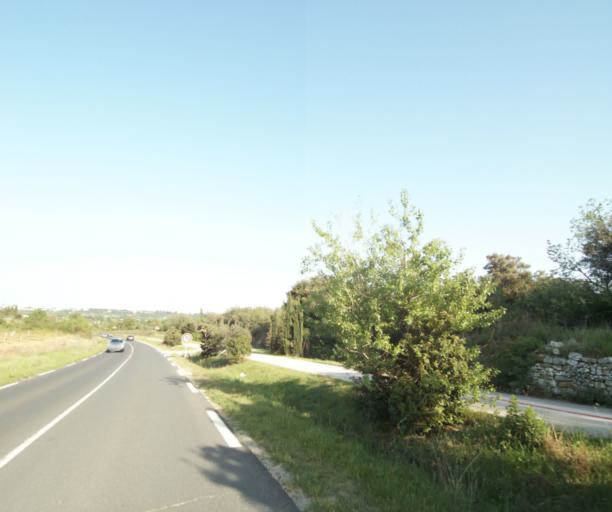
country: FR
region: Languedoc-Roussillon
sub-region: Departement de l'Herault
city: Juvignac
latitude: 43.6085
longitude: 3.7917
